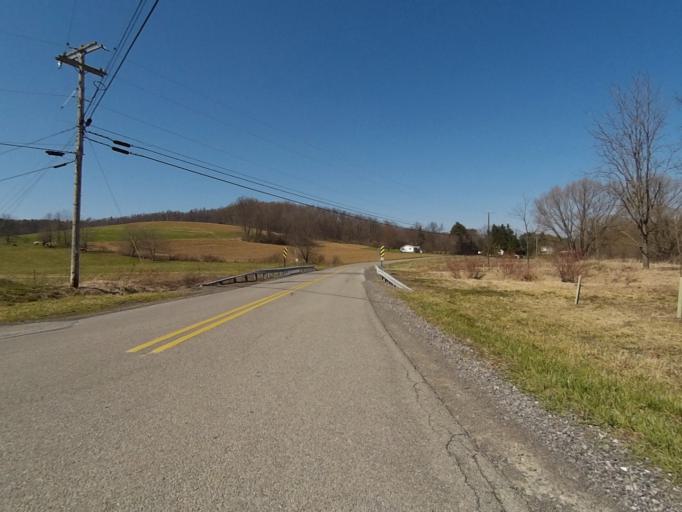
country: US
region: Pennsylvania
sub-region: Centre County
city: Stormstown
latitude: 40.7536
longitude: -78.0377
